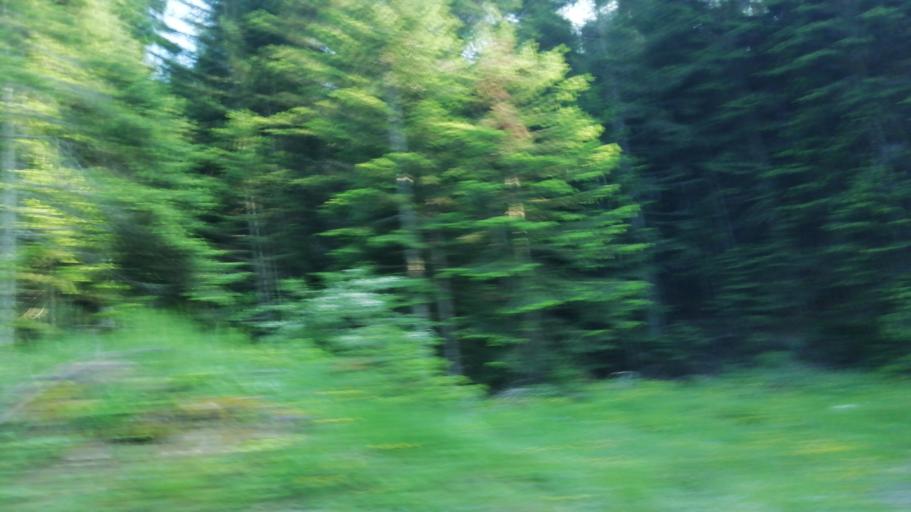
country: TR
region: Karabuk
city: Eskipazar
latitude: 41.0502
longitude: 32.5415
